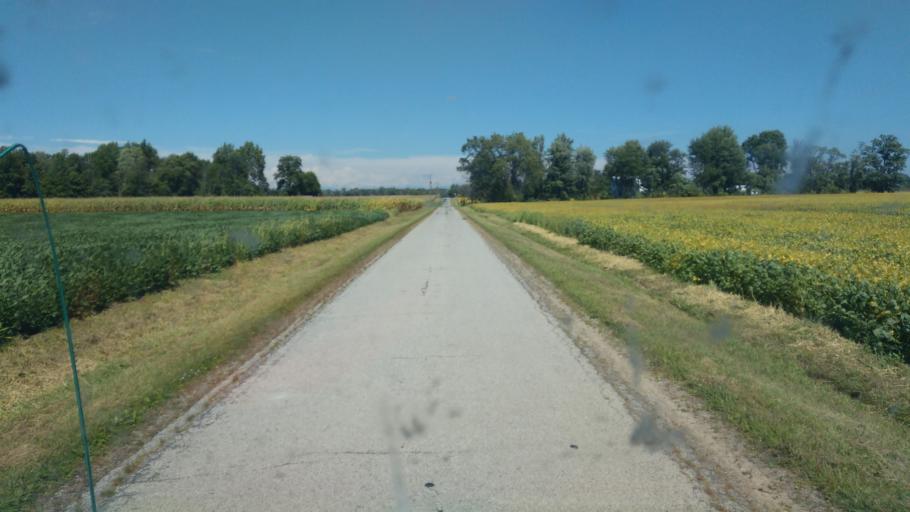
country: US
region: Ohio
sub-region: Crawford County
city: Galion
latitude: 40.7905
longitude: -82.8730
